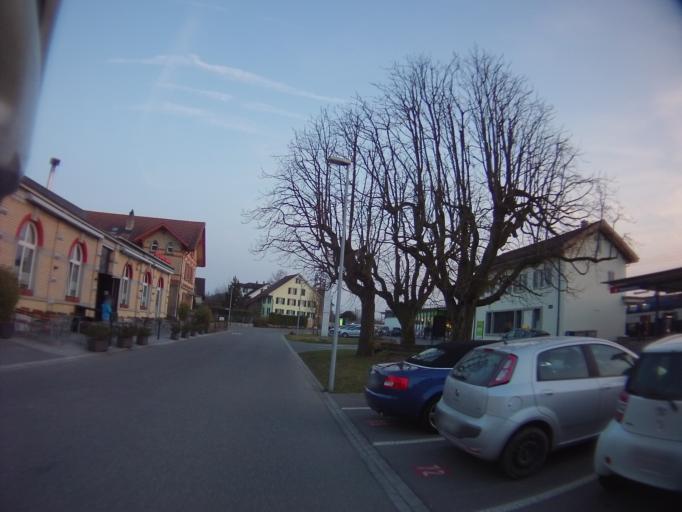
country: CH
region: Zurich
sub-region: Bezirk Affoltern
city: Mettmenstetten
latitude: 47.2445
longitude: 8.4576
